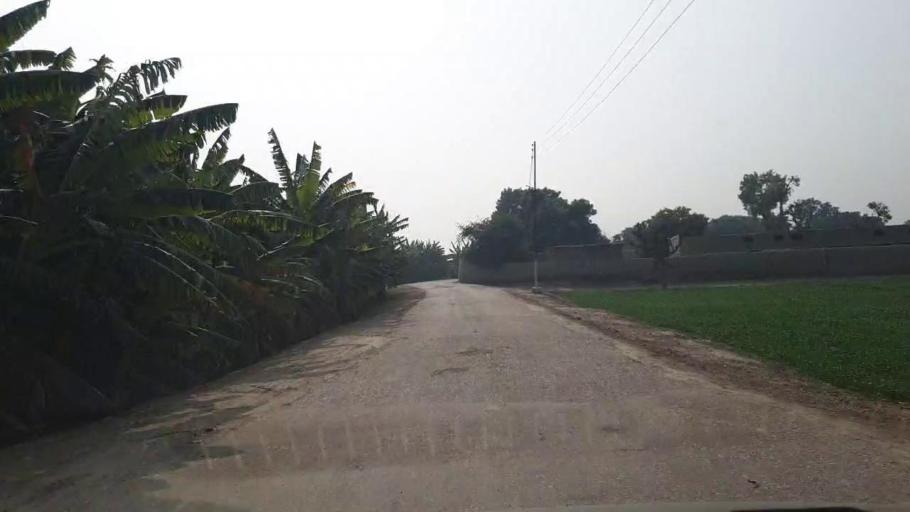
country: PK
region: Sindh
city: Hala
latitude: 25.8201
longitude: 68.4377
